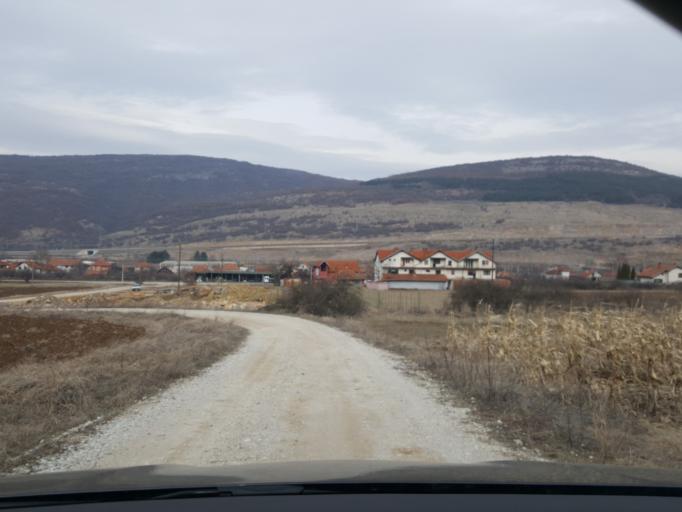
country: RS
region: Central Serbia
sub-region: Pirotski Okrug
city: Dimitrovgrad
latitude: 43.0088
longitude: 22.7466
